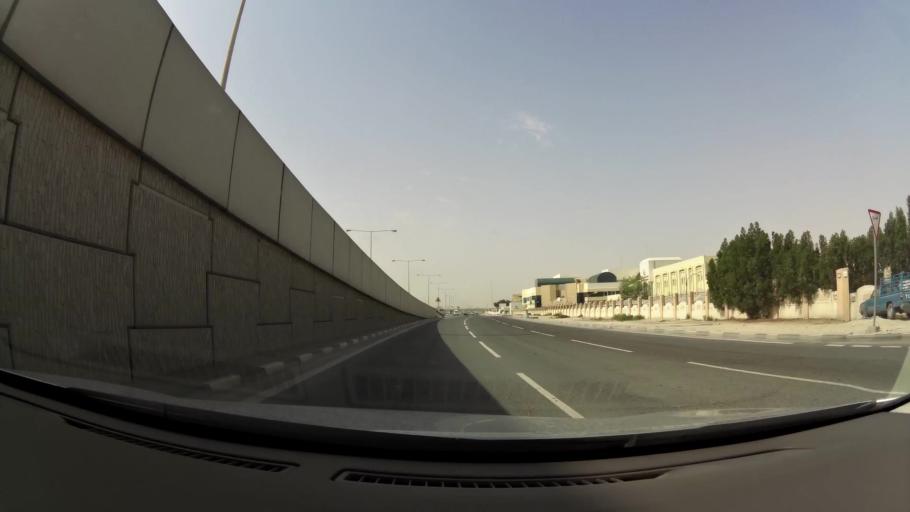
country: QA
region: Baladiyat ad Dawhah
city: Doha
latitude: 25.2367
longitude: 51.5218
